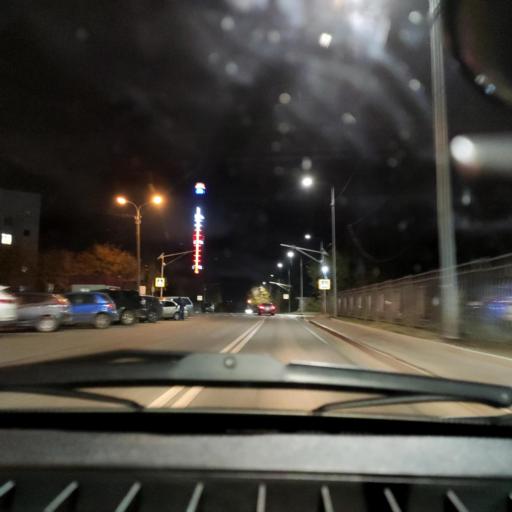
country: RU
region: Bashkortostan
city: Ufa
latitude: 54.7109
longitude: 56.0089
